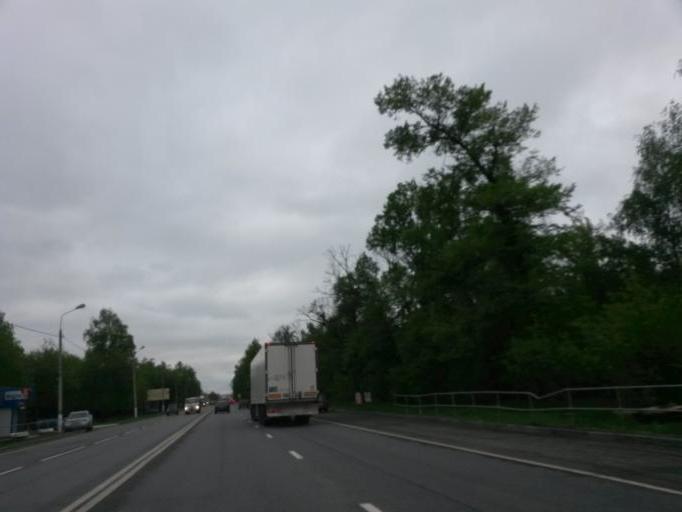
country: RU
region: Moskovskaya
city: Klimovsk
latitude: 55.3727
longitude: 37.5328
